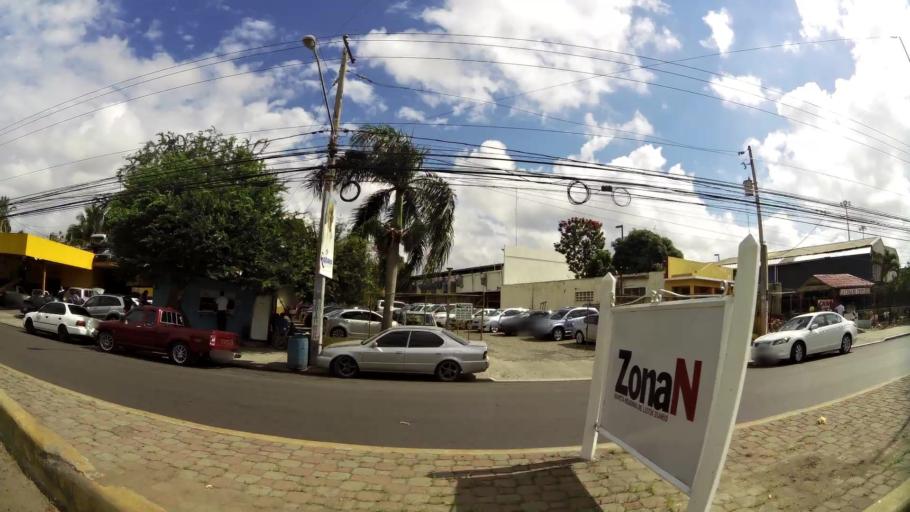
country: DO
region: Santiago
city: Santiago de los Caballeros
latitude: 19.4841
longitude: -70.7102
